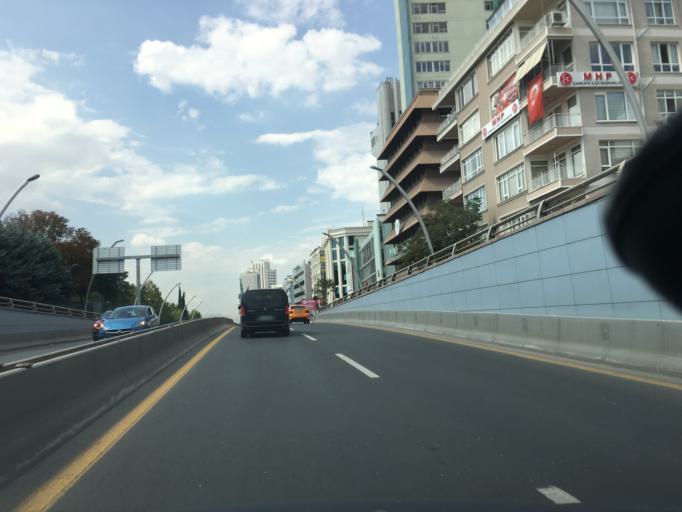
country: TR
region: Ankara
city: Cankaya
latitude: 39.9030
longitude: 32.8590
